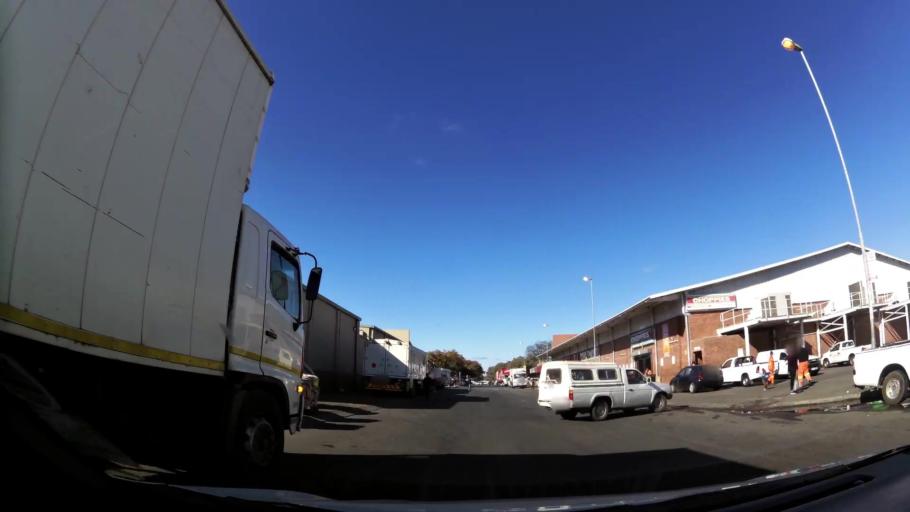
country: ZA
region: Limpopo
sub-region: Capricorn District Municipality
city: Polokwane
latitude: -23.9024
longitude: 29.4450
